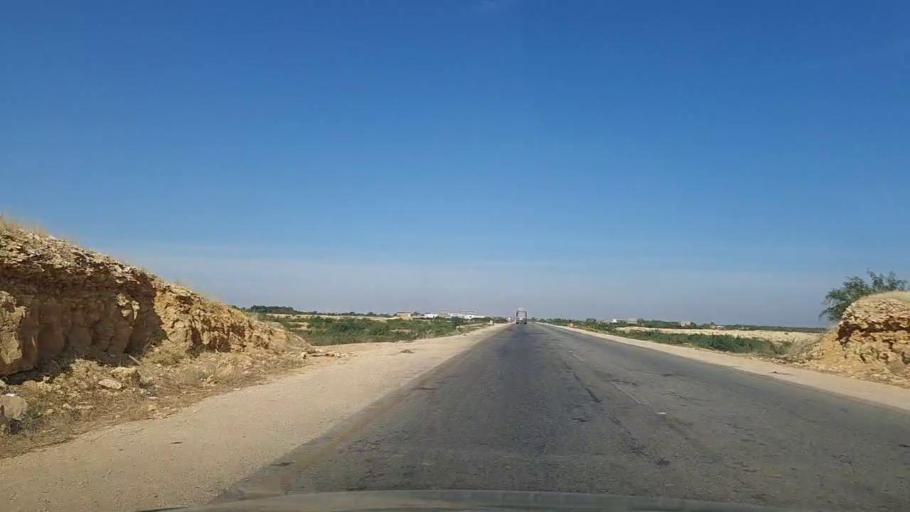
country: PK
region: Sindh
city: Kotri
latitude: 25.2108
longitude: 68.2376
